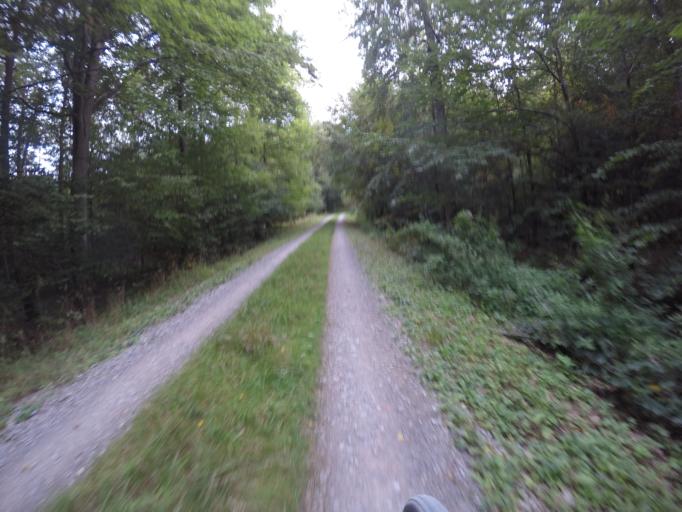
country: DE
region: Baden-Wuerttemberg
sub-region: Regierungsbezirk Stuttgart
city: Gerlingen
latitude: 48.7598
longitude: 9.0505
